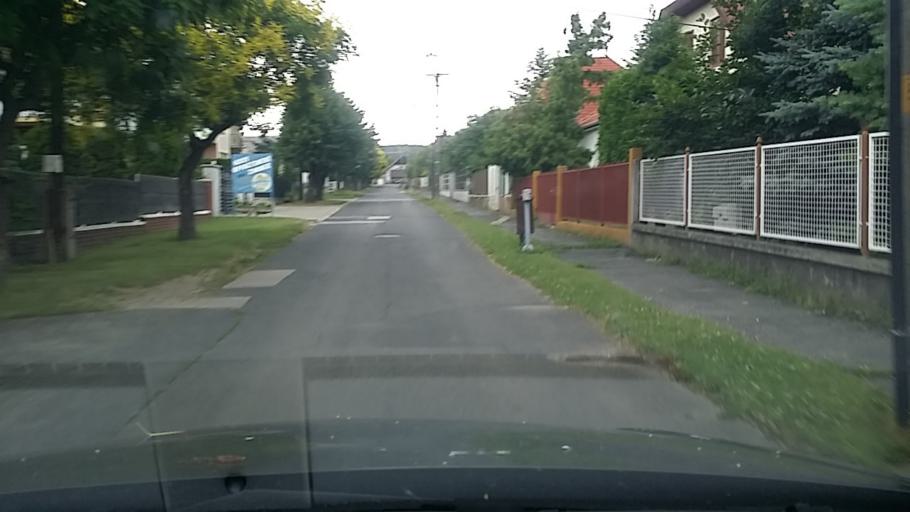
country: HU
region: Zala
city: Vonyarcvashegy
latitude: 46.7609
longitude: 17.3124
